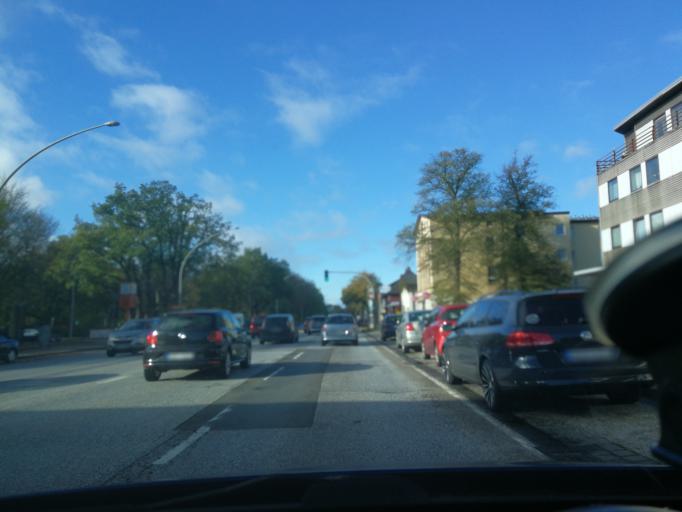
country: DE
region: Hamburg
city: Altona
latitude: 53.4719
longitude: 9.8897
